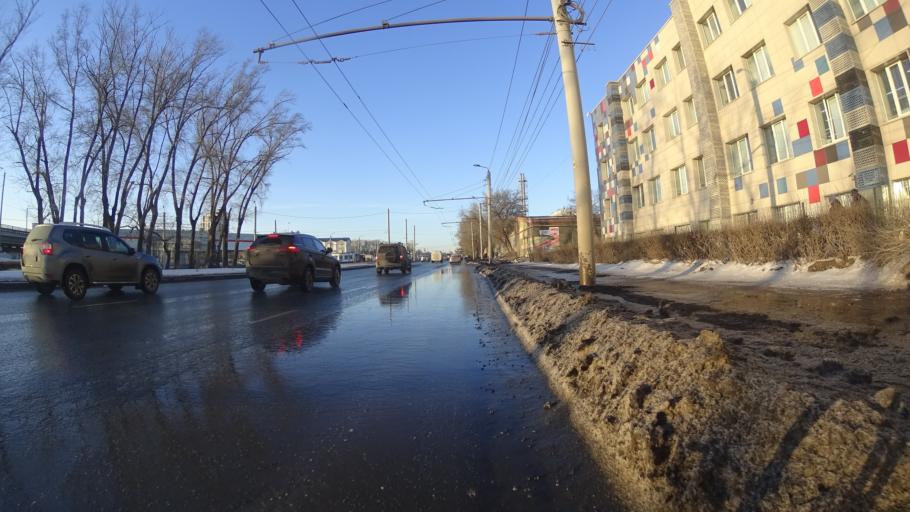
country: RU
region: Chelyabinsk
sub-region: Gorod Chelyabinsk
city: Chelyabinsk
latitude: 55.1558
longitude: 61.4447
